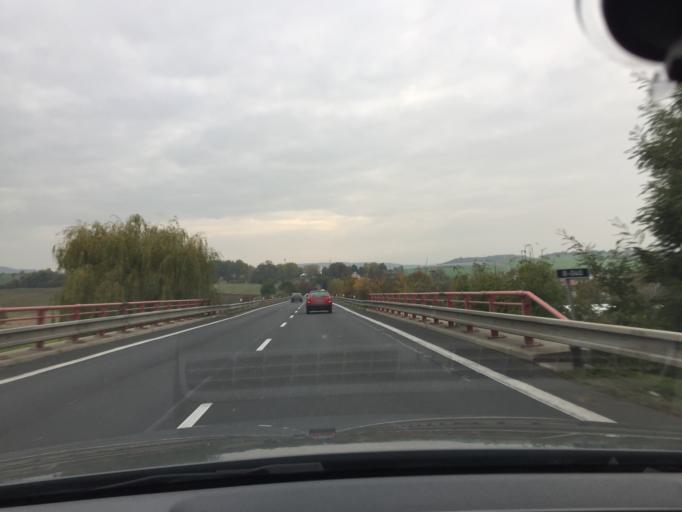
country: CZ
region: Ustecky
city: Rehlovice
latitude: 50.5875
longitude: 13.9106
